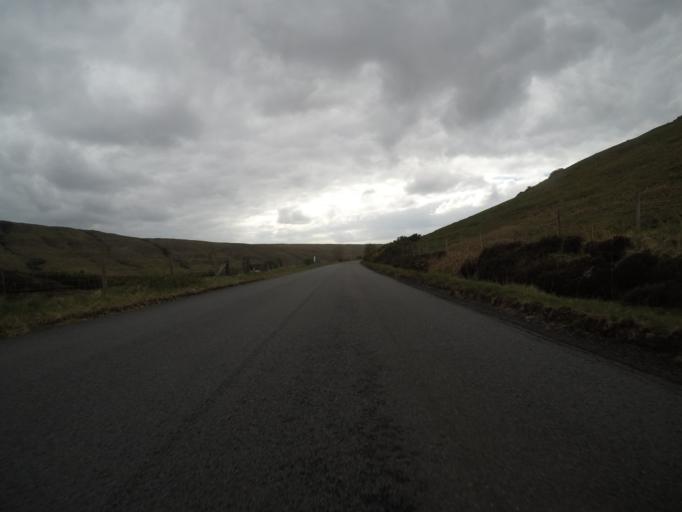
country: GB
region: Scotland
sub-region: Highland
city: Isle of Skye
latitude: 57.2980
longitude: -6.2616
